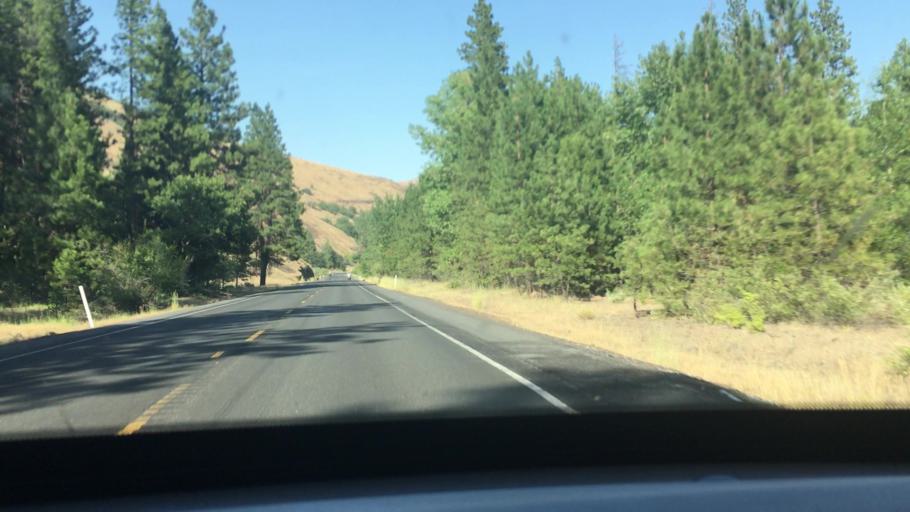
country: US
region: Washington
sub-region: Klickitat County
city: Goldendale
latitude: 46.0346
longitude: -120.5916
